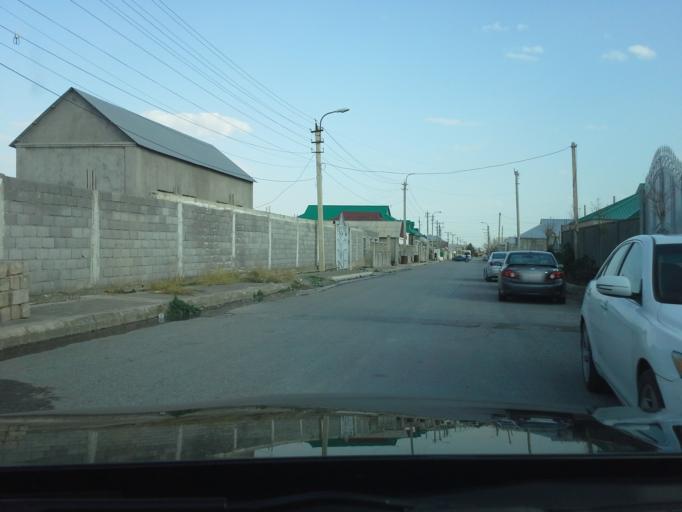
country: TM
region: Ahal
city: Abadan
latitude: 38.0216
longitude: 58.2237
